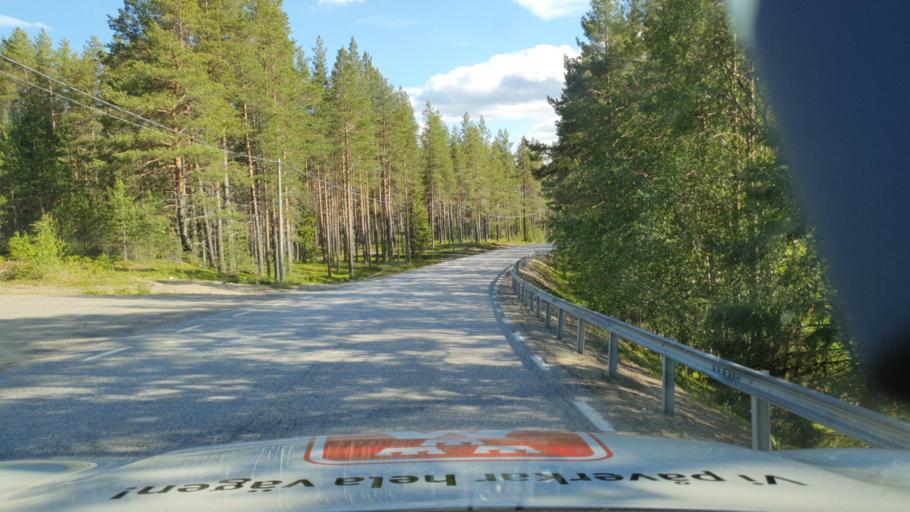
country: SE
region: Vaesterbotten
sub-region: Skelleftea Kommun
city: Langsele
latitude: 64.7763
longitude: 20.0186
